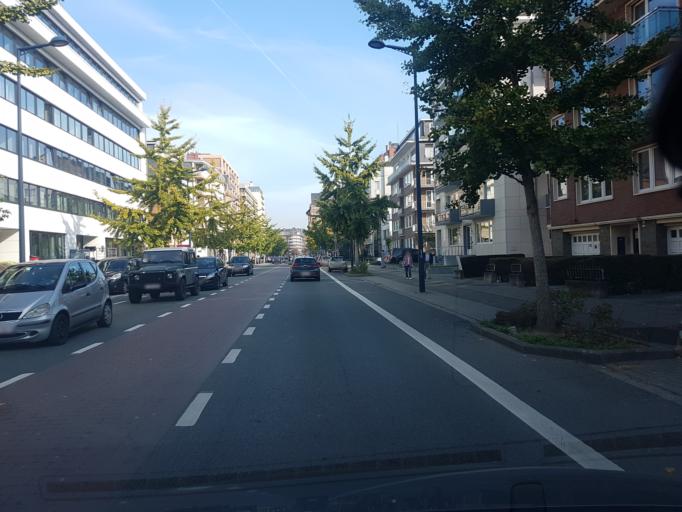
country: BE
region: Wallonia
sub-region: Province de Namur
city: Namur
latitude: 50.4577
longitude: 4.8733
